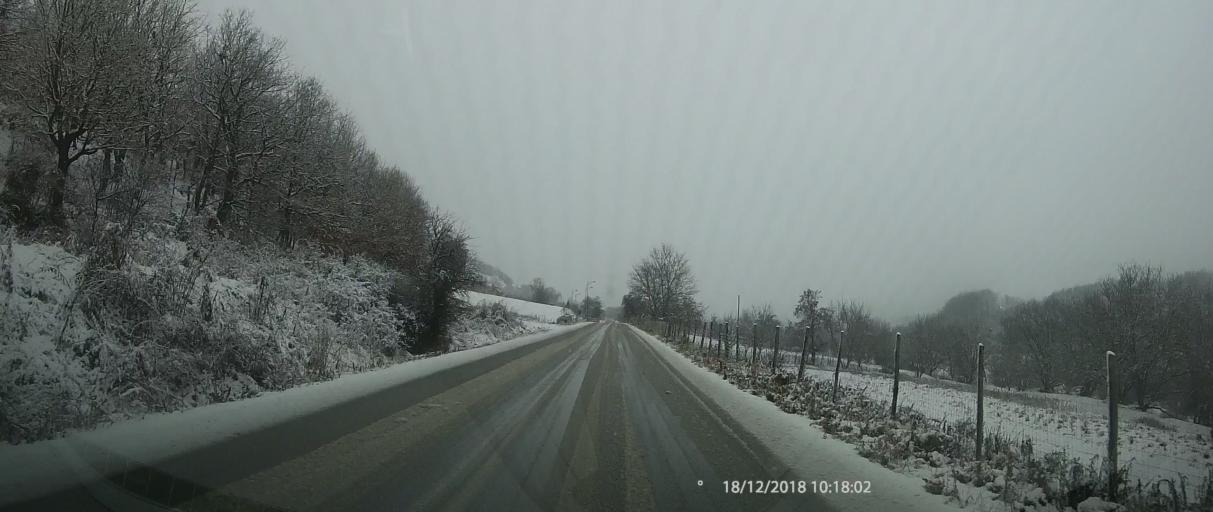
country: GR
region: Thessaly
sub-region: Nomos Larisis
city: Livadi
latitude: 40.1285
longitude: 22.2149
